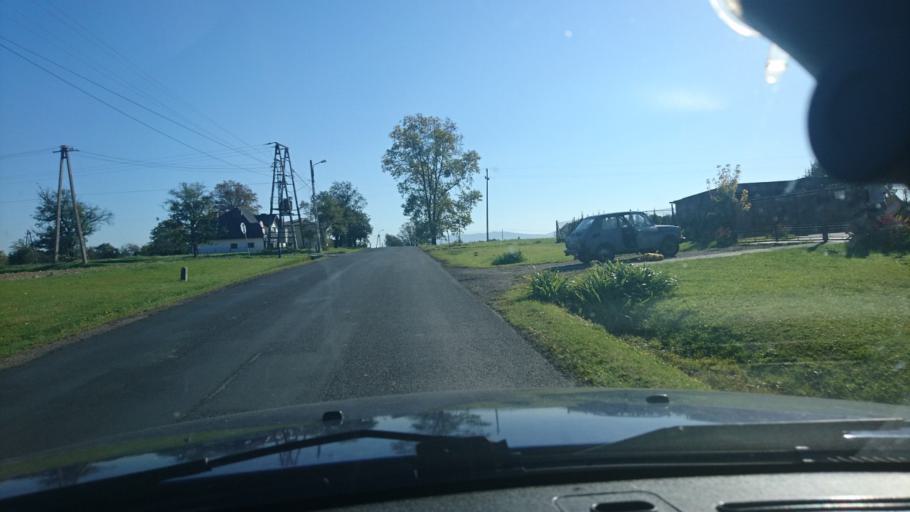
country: PL
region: Silesian Voivodeship
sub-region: Powiat bielski
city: Bronow
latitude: 49.8576
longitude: 18.9101
